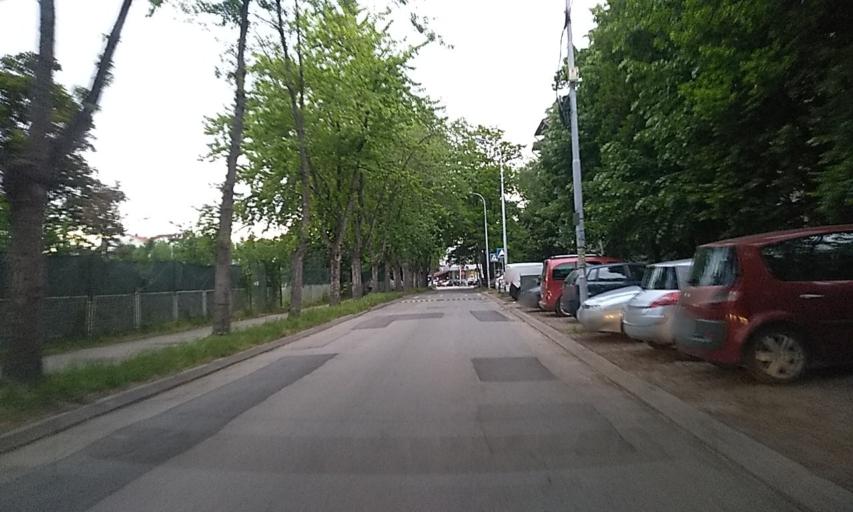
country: RS
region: Central Serbia
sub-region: Nisavski Okrug
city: Nis
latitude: 43.3216
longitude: 21.9214
